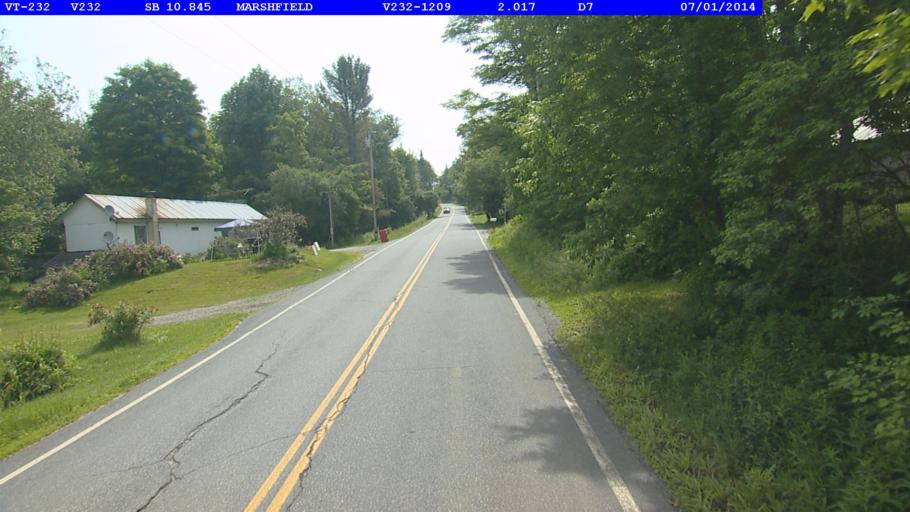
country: US
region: Vermont
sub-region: Caledonia County
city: Hardwick
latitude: 44.3392
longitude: -72.2886
